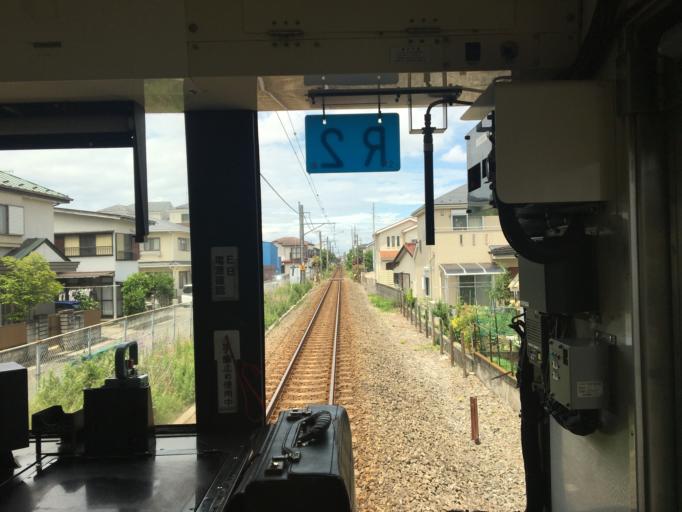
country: JP
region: Kanagawa
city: Chigasaki
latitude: 35.3527
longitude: 139.4007
